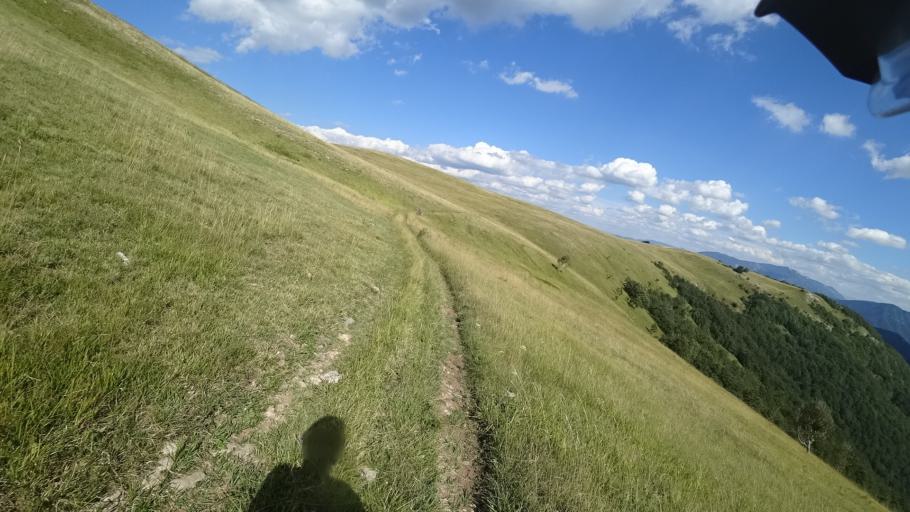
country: HR
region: Zadarska
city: Gracac
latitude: 44.3711
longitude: 16.0622
